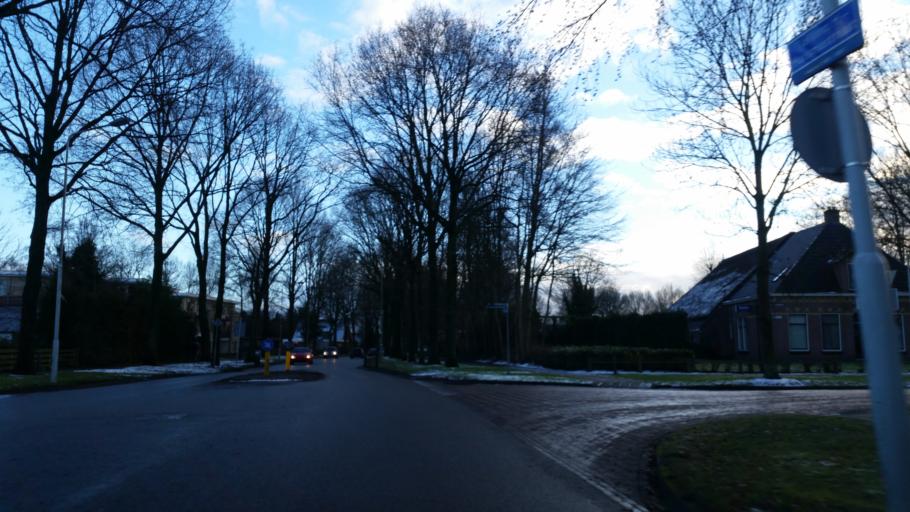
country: NL
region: Friesland
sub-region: Gemeente Tytsjerksteradiel
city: Burgum
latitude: 53.1943
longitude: 5.9965
